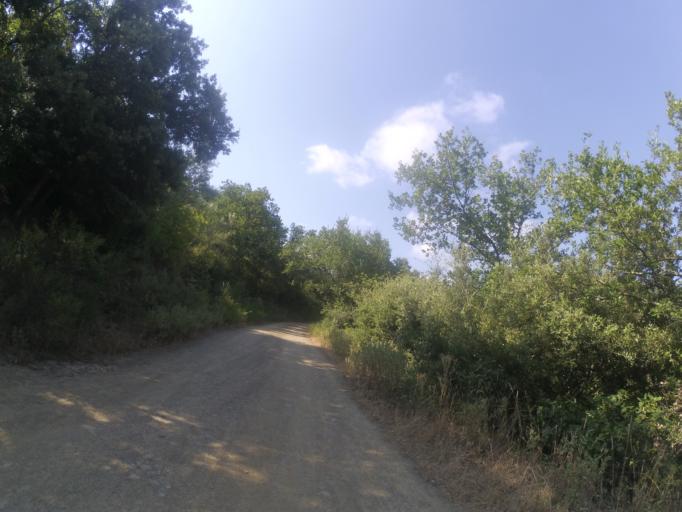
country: FR
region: Languedoc-Roussillon
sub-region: Departement des Pyrenees-Orientales
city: Ille-sur-Tet
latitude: 42.6476
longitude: 2.6275
